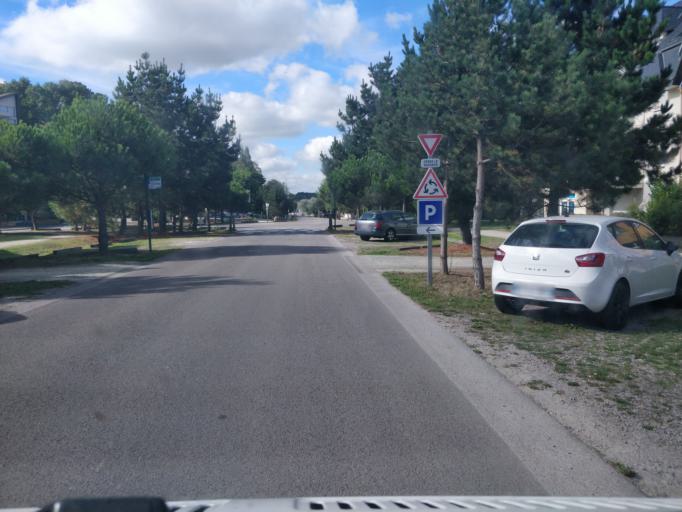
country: FR
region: Brittany
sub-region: Departement des Cotes-d'Armor
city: Plurien
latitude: 48.6380
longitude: -2.4063
